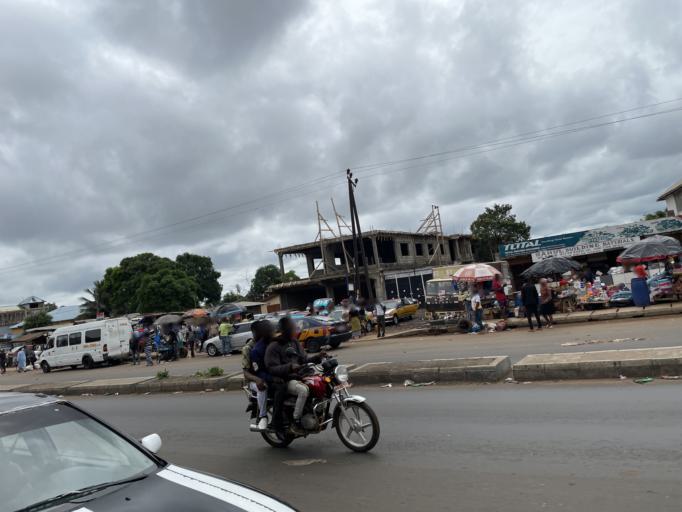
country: SL
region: Western Area
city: Hastings
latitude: 8.3915
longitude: -13.1438
